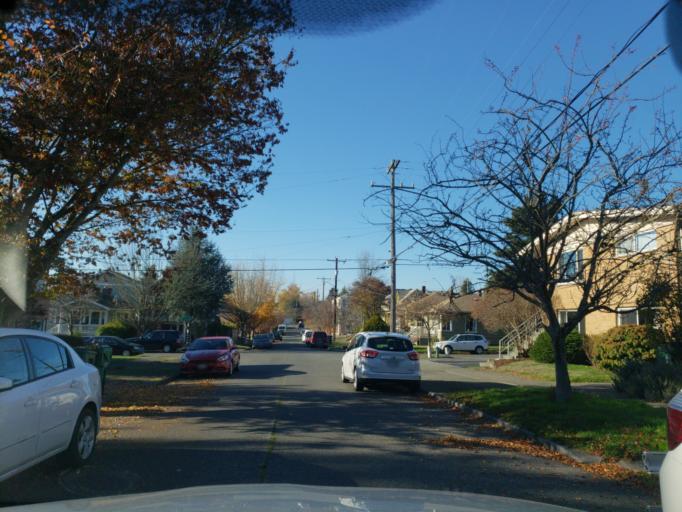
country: US
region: Washington
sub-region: King County
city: Seattle
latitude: 47.6742
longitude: -122.3635
